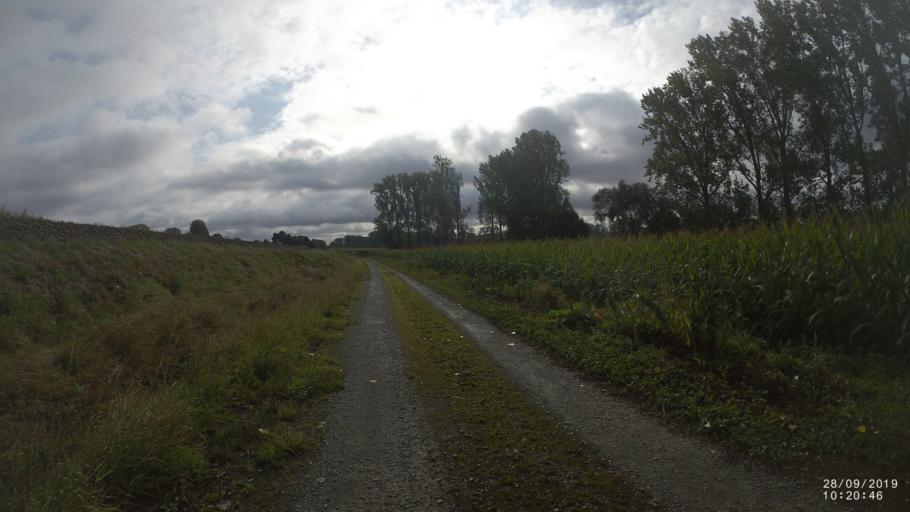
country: BE
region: Flanders
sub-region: Provincie Oost-Vlaanderen
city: Sint-Maria-Lierde
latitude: 50.8069
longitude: 3.8391
